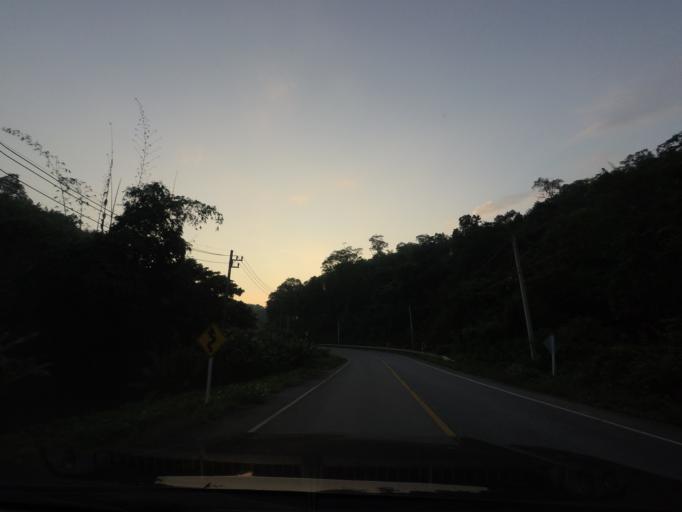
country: TH
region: Nan
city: Na Noi
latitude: 18.4226
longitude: 100.7027
